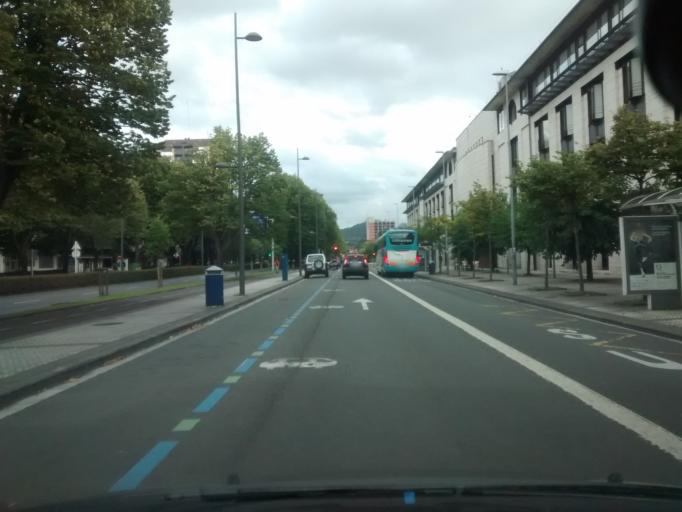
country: ES
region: Basque Country
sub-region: Provincia de Guipuzcoa
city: San Sebastian
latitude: 43.3080
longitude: -2.0096
